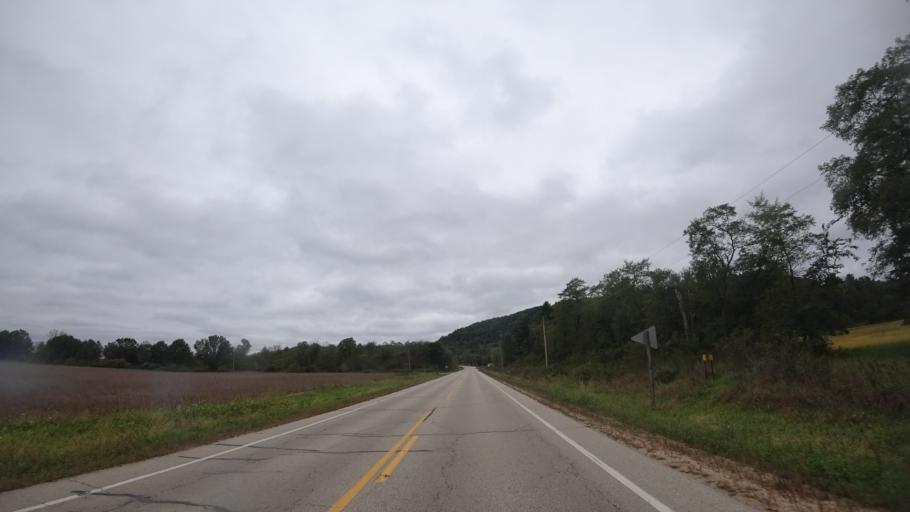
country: US
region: Wisconsin
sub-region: Grant County
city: Boscobel
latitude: 43.2053
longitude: -90.6354
